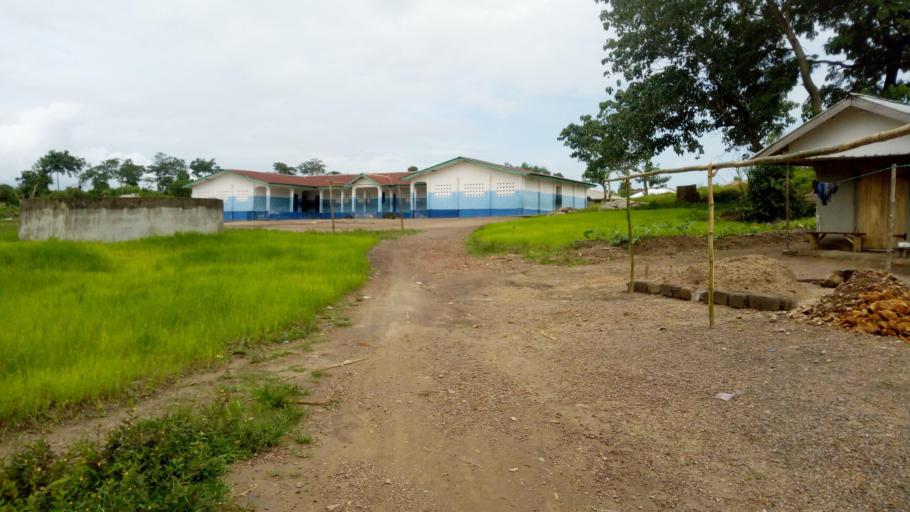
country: SL
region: Northern Province
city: Magburaka
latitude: 8.7133
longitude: -11.9612
